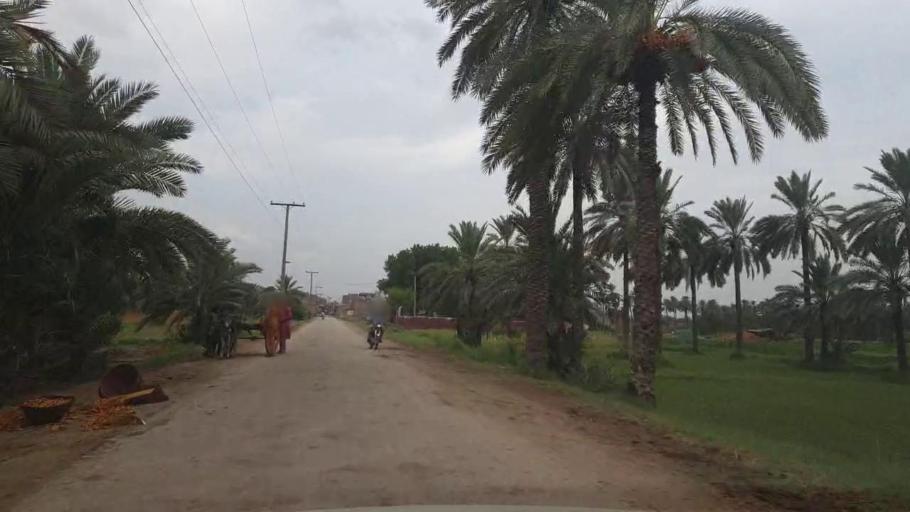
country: PK
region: Sindh
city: Khairpur
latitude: 27.5420
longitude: 68.7433
